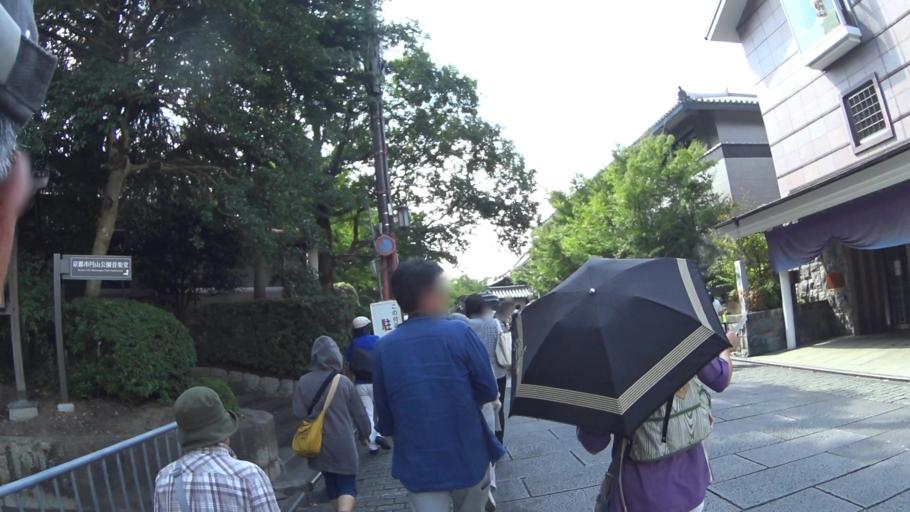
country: JP
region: Kyoto
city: Kyoto
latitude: 35.0027
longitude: 135.7808
